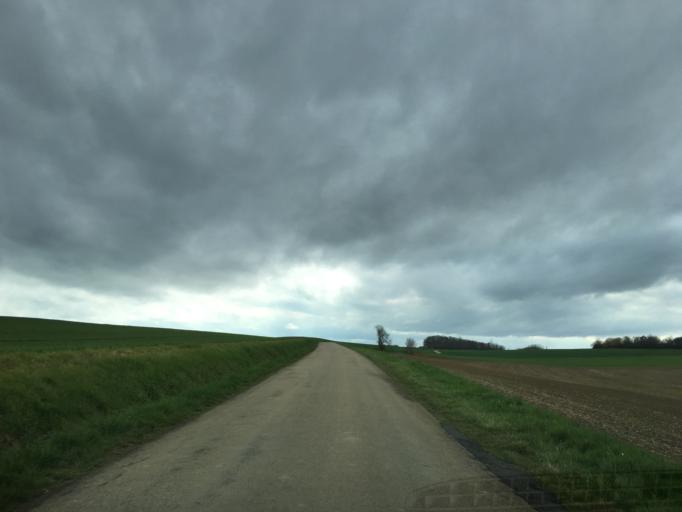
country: FR
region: Bourgogne
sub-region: Departement de l'Yonne
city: Fleury-la-Vallee
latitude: 47.8511
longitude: 3.4281
